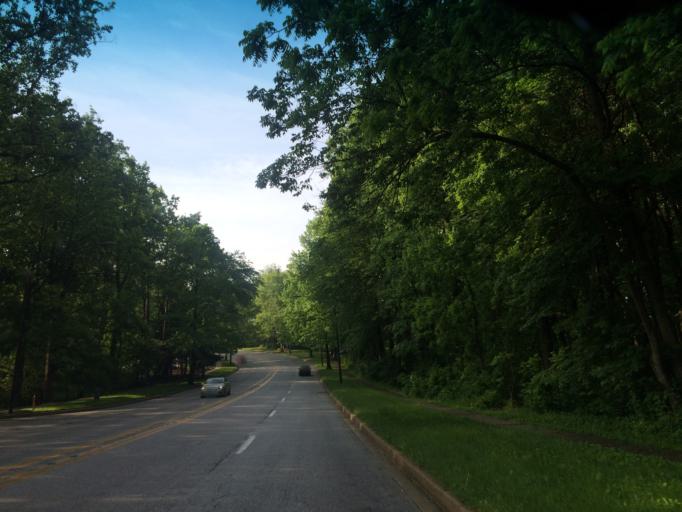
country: US
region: Maryland
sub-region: Howard County
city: Riverside
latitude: 39.2237
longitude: -76.8932
